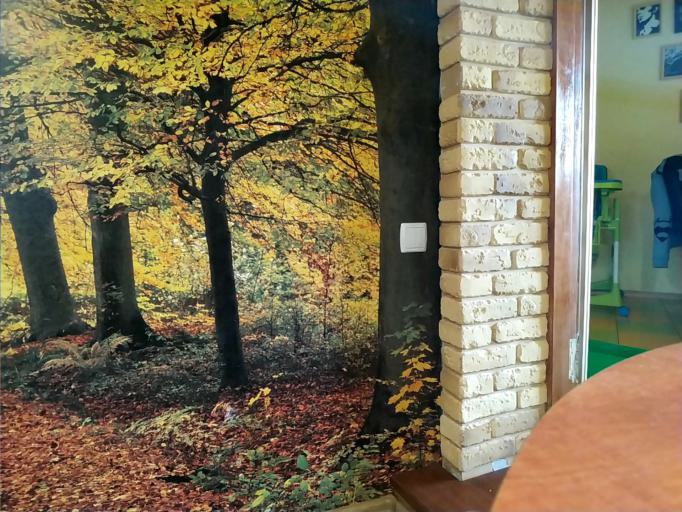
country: RU
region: Leningrad
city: Luga
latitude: 58.9674
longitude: 29.5591
